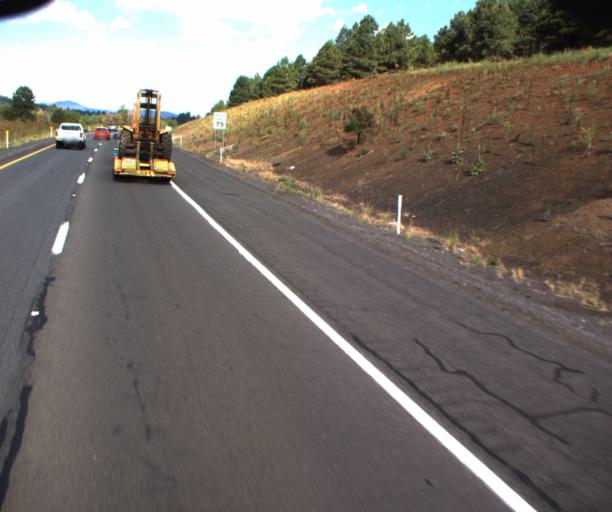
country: US
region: Arizona
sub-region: Coconino County
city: Flagstaff
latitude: 35.1996
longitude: -111.7523
